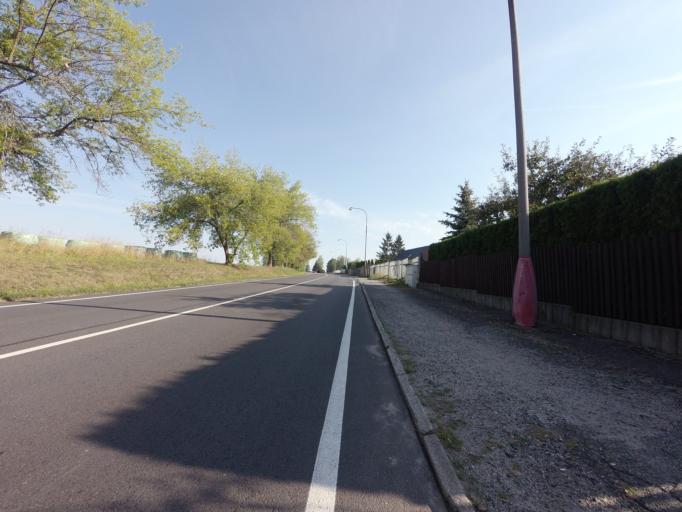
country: CZ
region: Jihocesky
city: Tyn nad Vltavou
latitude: 49.2314
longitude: 14.4214
